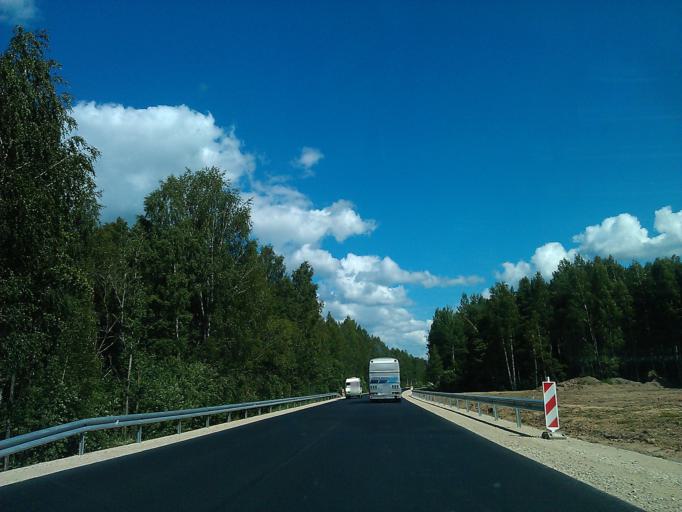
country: LV
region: Vilanu
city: Vilani
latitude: 56.5623
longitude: 27.0197
